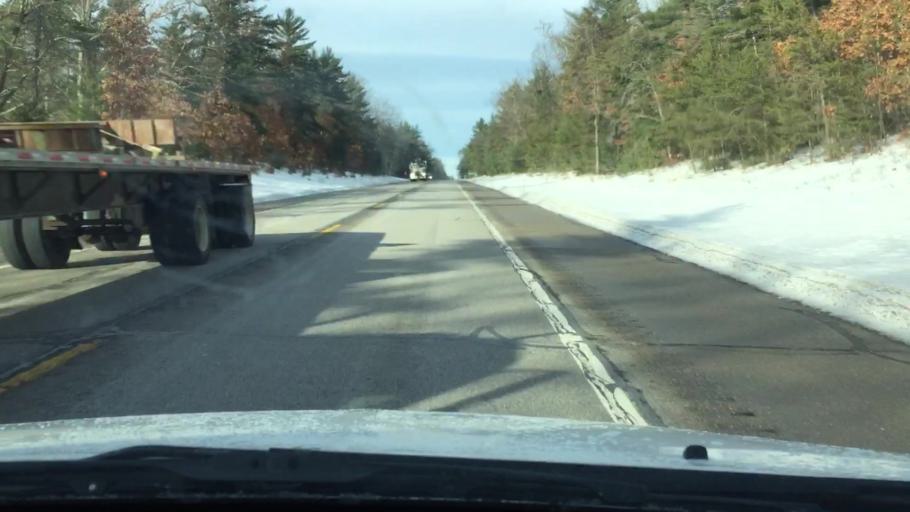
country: US
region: Michigan
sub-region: Wexford County
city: Manton
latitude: 44.5508
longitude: -85.3695
